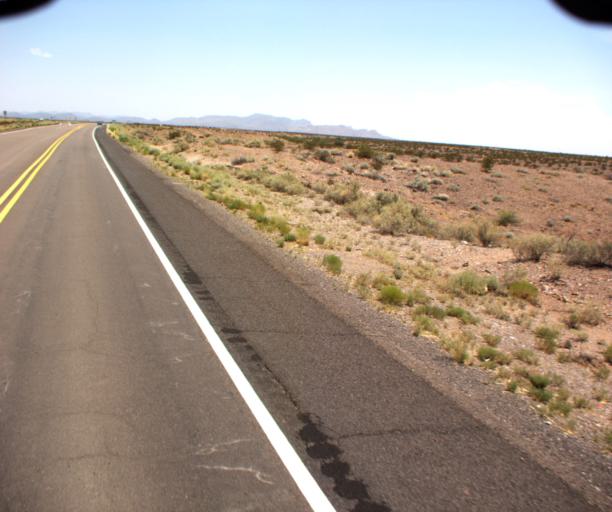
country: US
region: Arizona
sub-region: Graham County
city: Safford
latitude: 32.7948
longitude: -109.5556
